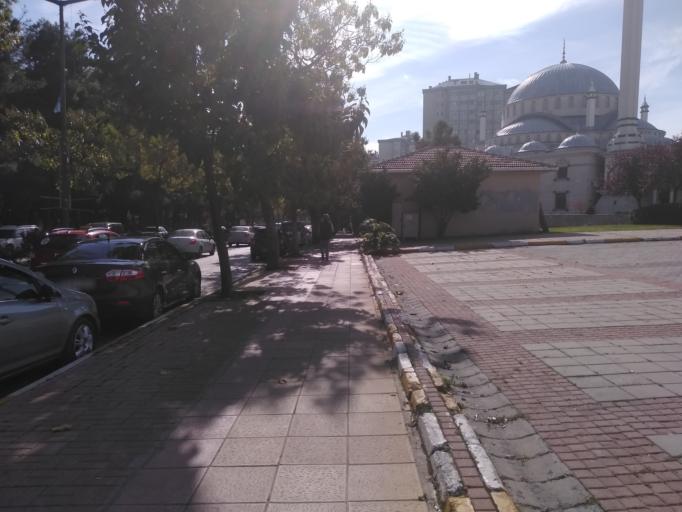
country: TR
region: Istanbul
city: Beylikduezue
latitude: 41.0102
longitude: 28.6436
